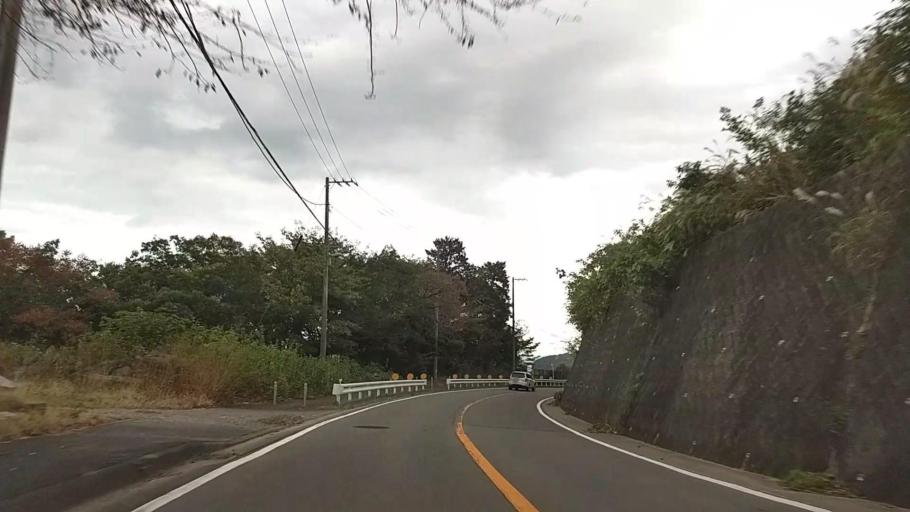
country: JP
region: Kanagawa
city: Yugawara
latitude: 35.1711
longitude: 139.1332
